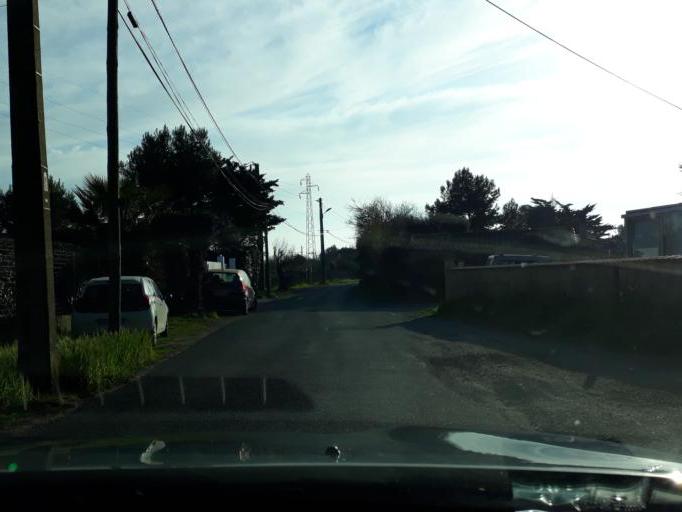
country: FR
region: Languedoc-Roussillon
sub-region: Departement de l'Herault
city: Marseillan
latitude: 43.3232
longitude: 3.5436
